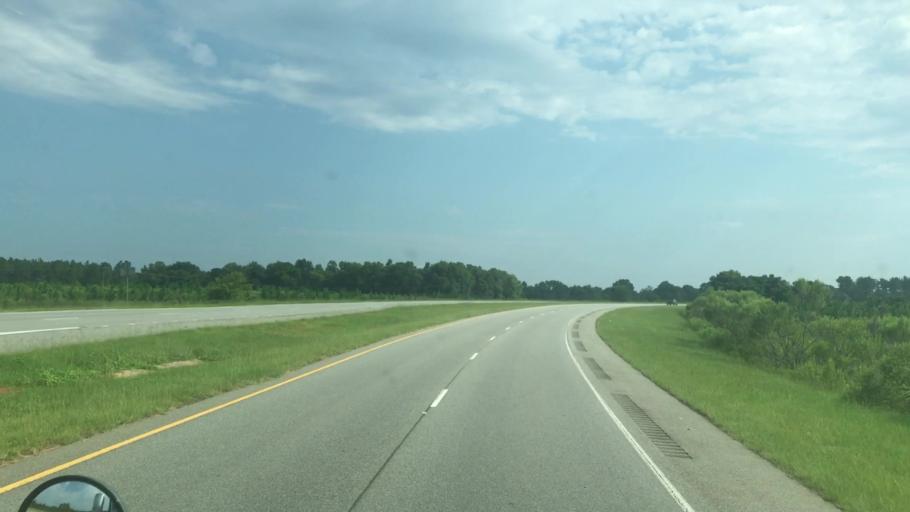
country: US
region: Georgia
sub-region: Early County
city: Blakely
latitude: 31.3598
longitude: -84.9233
